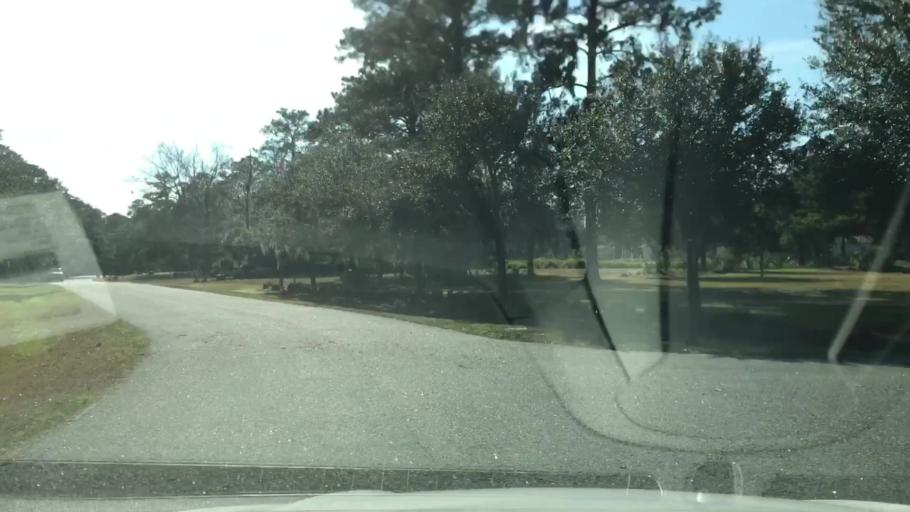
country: US
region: South Carolina
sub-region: Beaufort County
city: Bluffton
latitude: 32.3382
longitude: -80.9073
